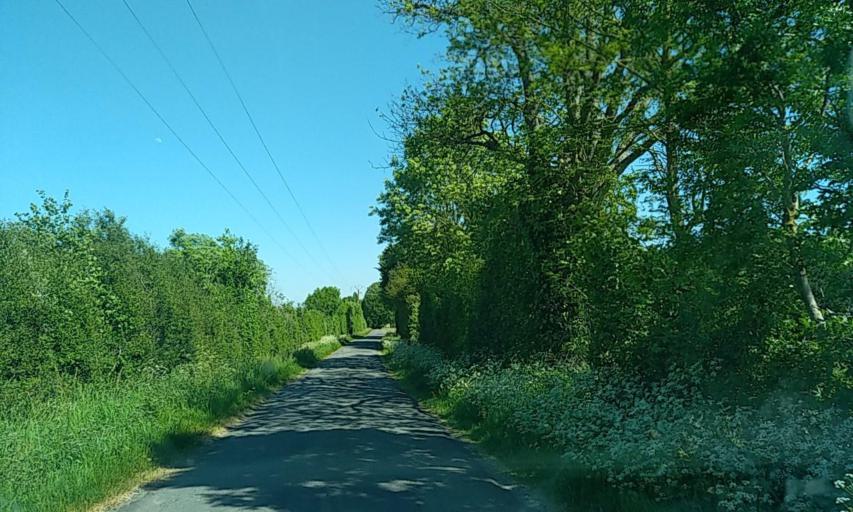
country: FR
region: Poitou-Charentes
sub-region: Departement des Deux-Sevres
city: Boisme
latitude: 46.7686
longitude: -0.4589
